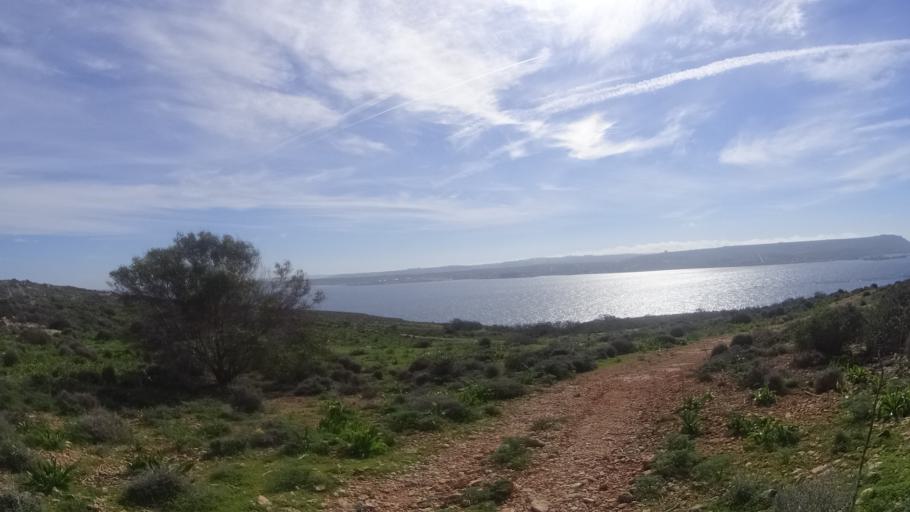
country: MT
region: Il-Qala
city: Qala
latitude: 36.0080
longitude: 14.3337
